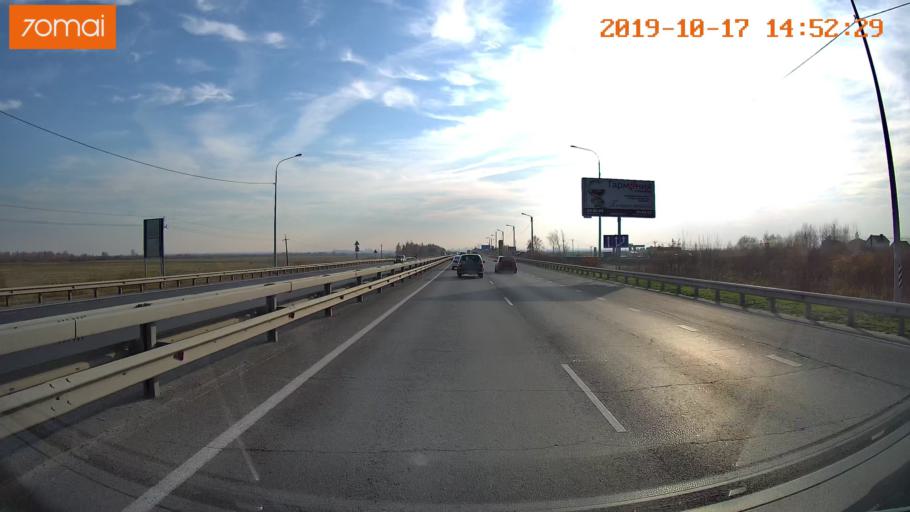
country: RU
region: Rjazan
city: Polyany
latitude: 54.7065
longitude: 39.8453
